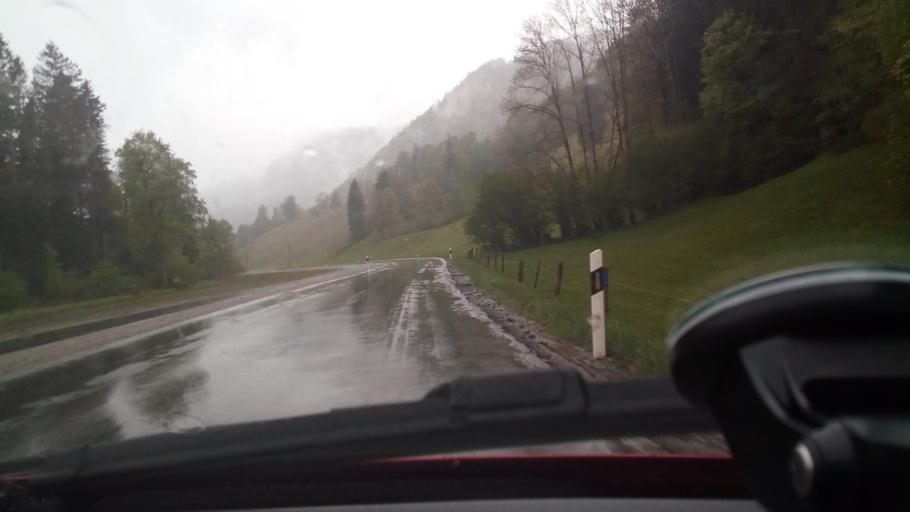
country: DE
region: Bavaria
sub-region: Upper Bavaria
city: Lenggries
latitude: 47.6301
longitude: 11.5382
